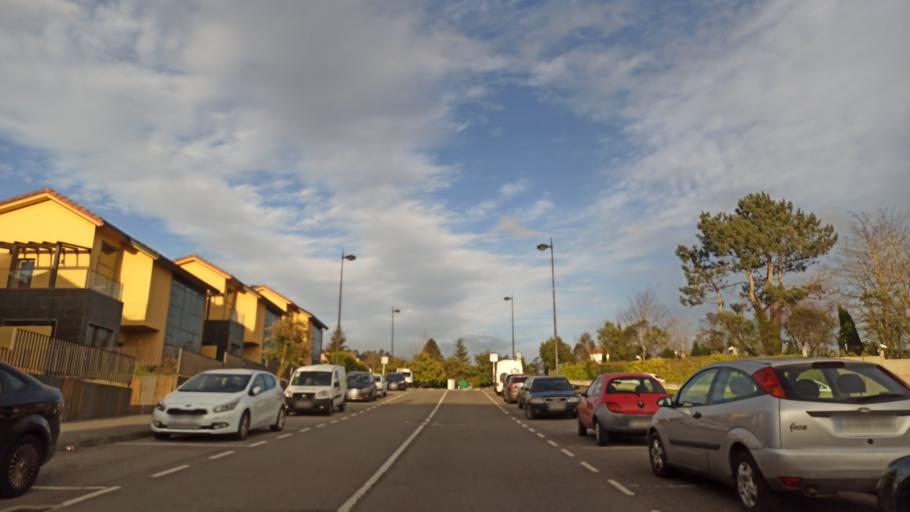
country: ES
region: Galicia
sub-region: Provincia da Coruna
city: Cambre
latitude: 43.3226
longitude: -8.3510
